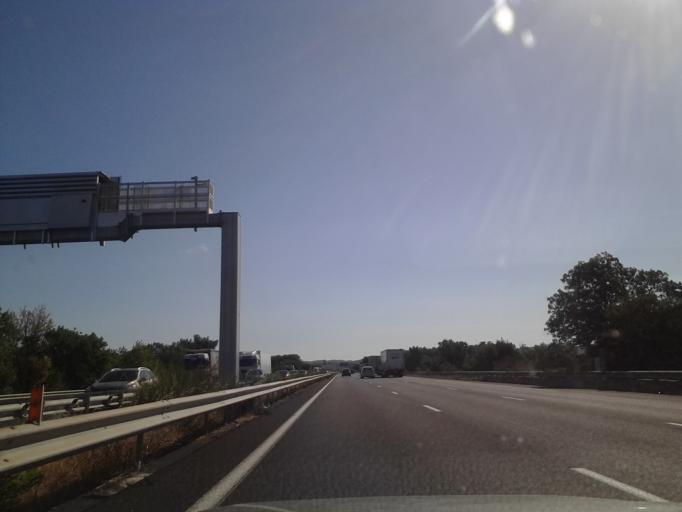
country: FR
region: Languedoc-Roussillon
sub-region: Departement de l'Aude
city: Narbonne
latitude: 43.1722
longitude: 3.0207
